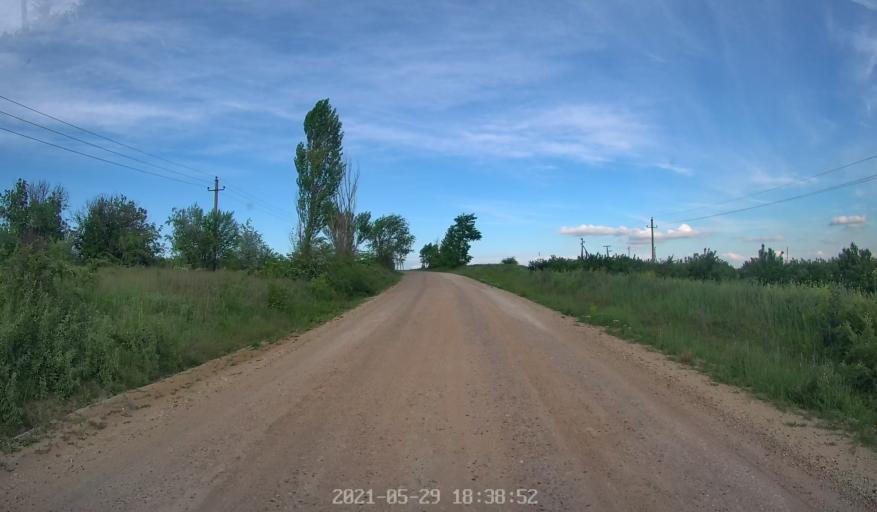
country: MD
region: Chisinau
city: Singera
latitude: 46.8012
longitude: 28.9406
